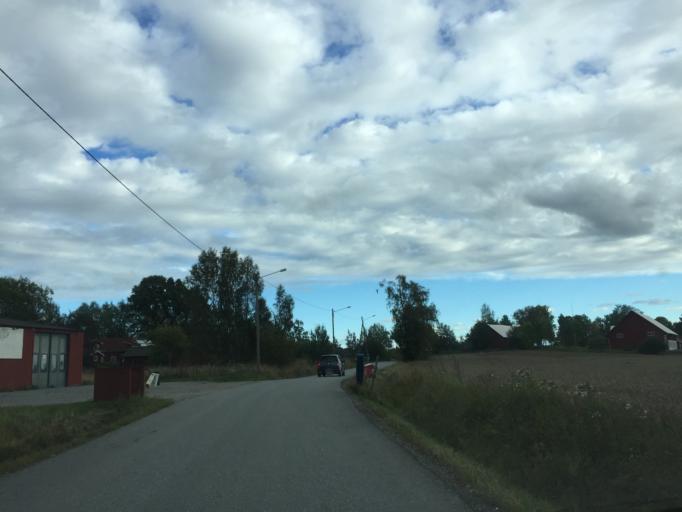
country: SE
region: OErebro
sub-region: Orebro Kommun
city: Hovsta
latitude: 59.3221
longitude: 15.2045
